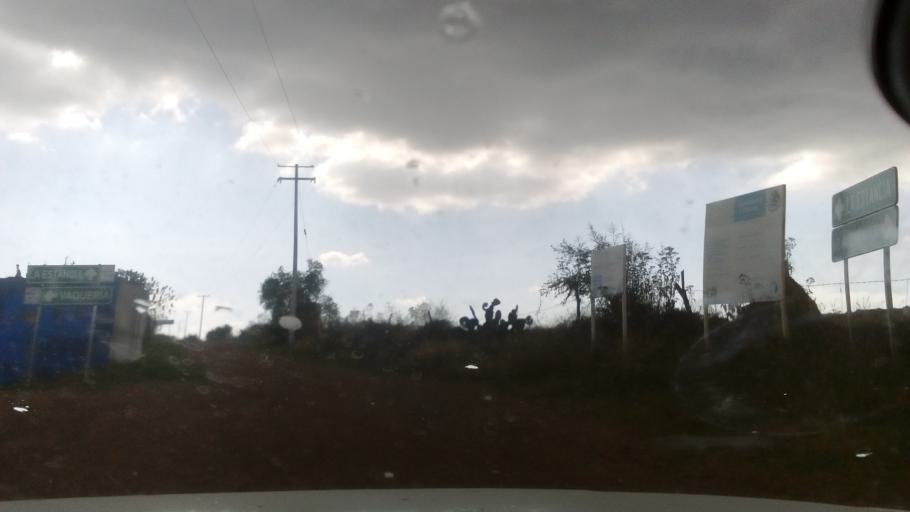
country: MX
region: Guanajuato
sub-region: Silao de la Victoria
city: San Francisco (Banos de Agua Caliente)
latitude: 21.1668
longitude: -101.4170
